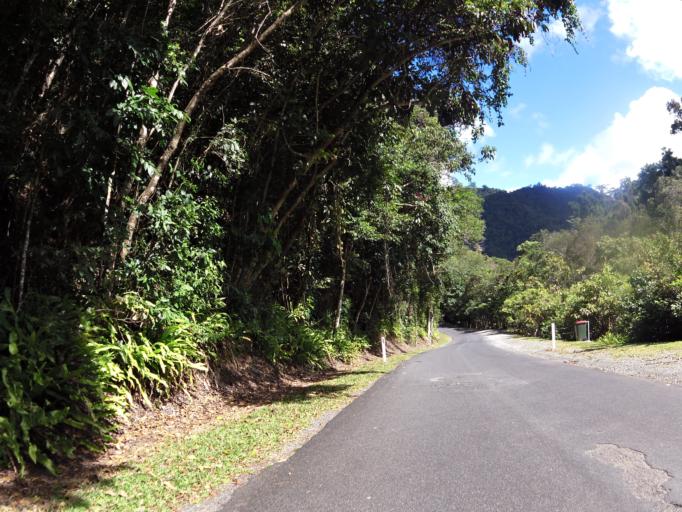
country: AU
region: Queensland
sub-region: Cairns
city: Woree
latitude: -16.9591
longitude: 145.6831
